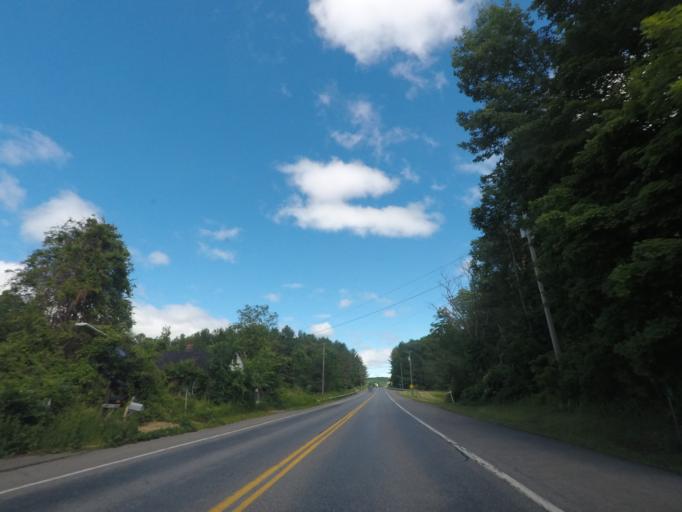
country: US
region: New York
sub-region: Columbia County
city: Philmont
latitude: 42.2093
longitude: -73.6436
